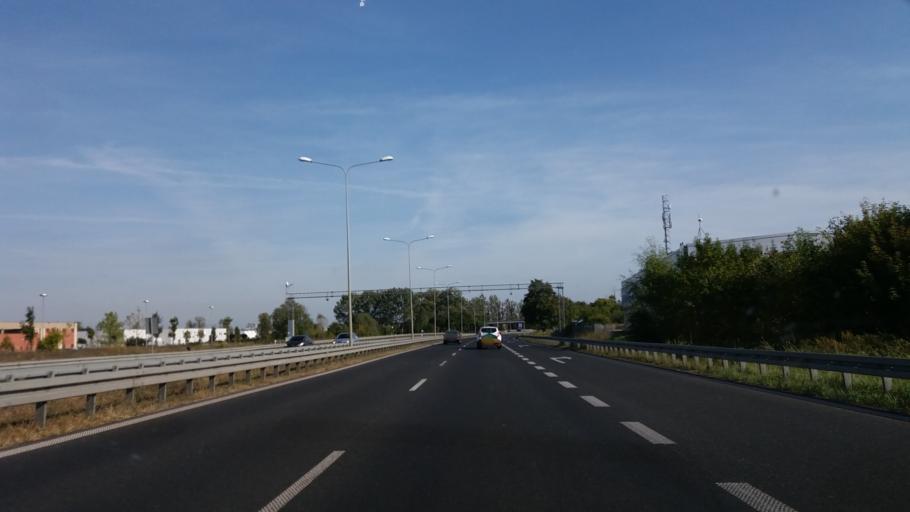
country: PL
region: Greater Poland Voivodeship
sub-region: Powiat poznanski
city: Baranowo
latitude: 52.4413
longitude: 16.7486
